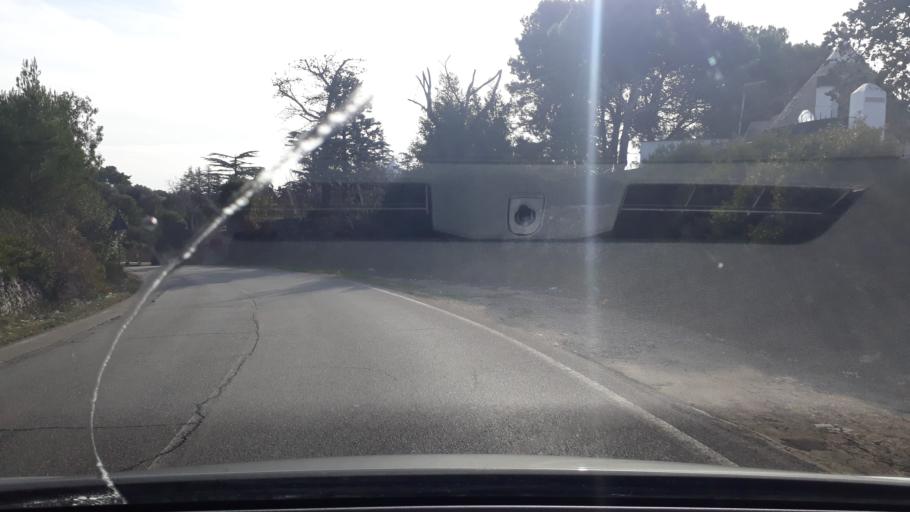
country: IT
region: Apulia
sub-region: Provincia di Taranto
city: Martina Franca
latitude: 40.6893
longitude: 17.3500
